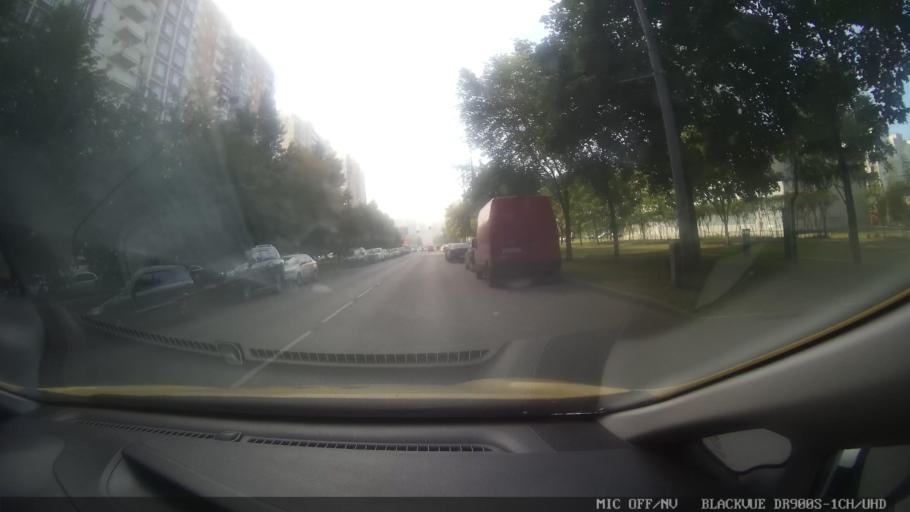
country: RU
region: Moscow
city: Zhulebino
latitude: 55.6838
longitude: 37.8623
